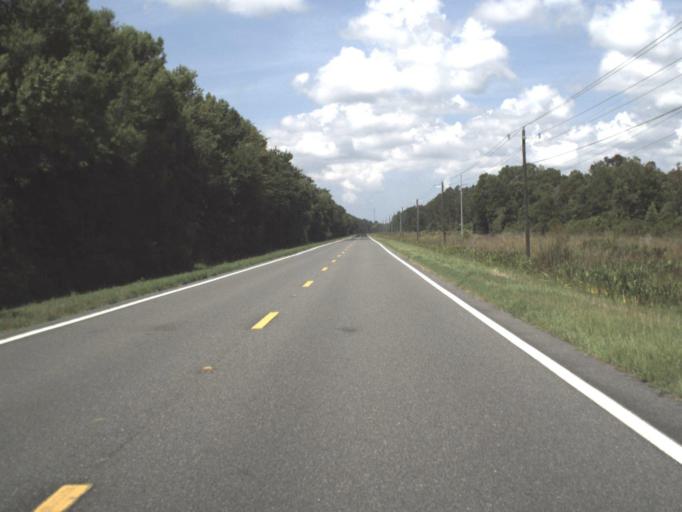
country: US
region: Florida
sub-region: Levy County
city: Chiefland
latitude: 29.2576
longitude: -82.8932
